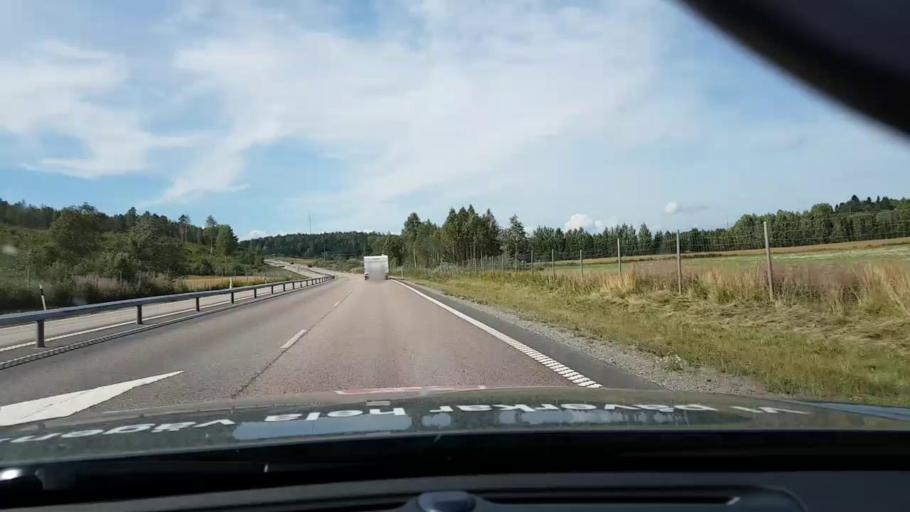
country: SE
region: Vaesternorrland
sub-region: OErnskoeldsviks Kommun
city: Ornskoldsvik
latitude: 63.3076
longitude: 18.8462
